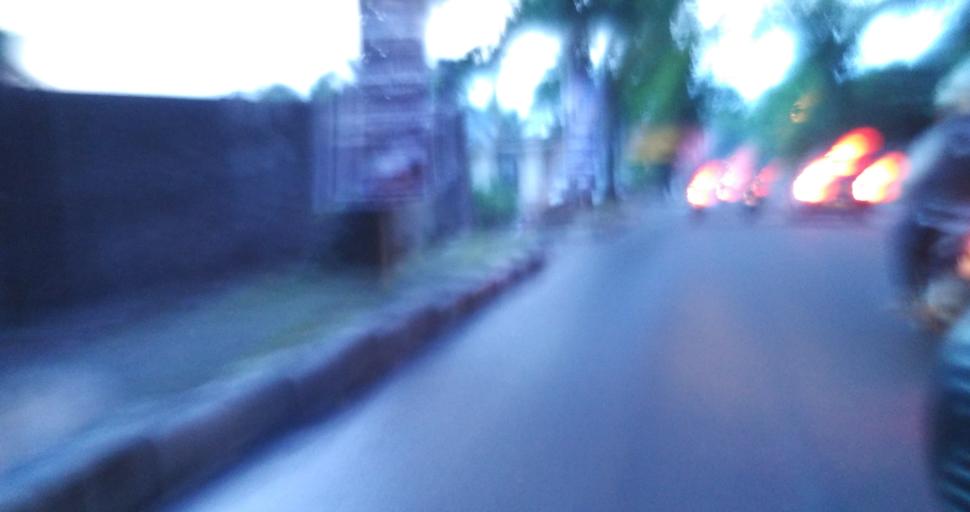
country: ID
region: Central Java
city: Semarang
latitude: -7.0401
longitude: 110.4191
